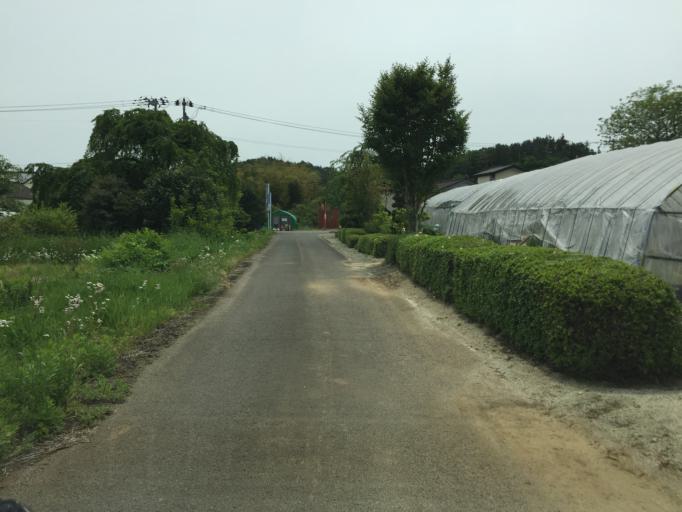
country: JP
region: Fukushima
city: Fukushima-shi
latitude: 37.7206
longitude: 140.3990
